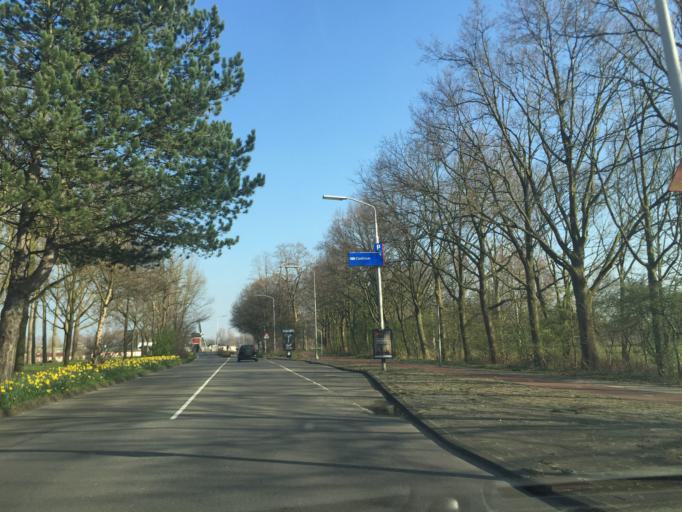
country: NL
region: South Holland
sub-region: Gemeente Oegstgeest
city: Oegstgeest
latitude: 52.1779
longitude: 4.4845
